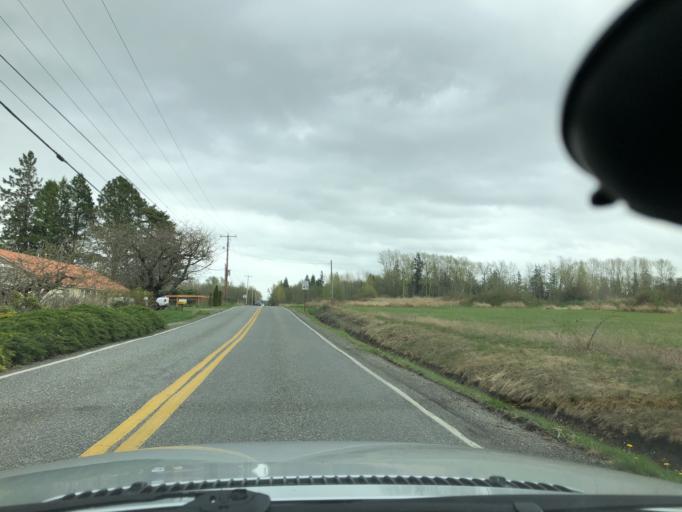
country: US
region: Washington
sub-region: Whatcom County
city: Birch Bay
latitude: 48.8925
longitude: -122.7706
